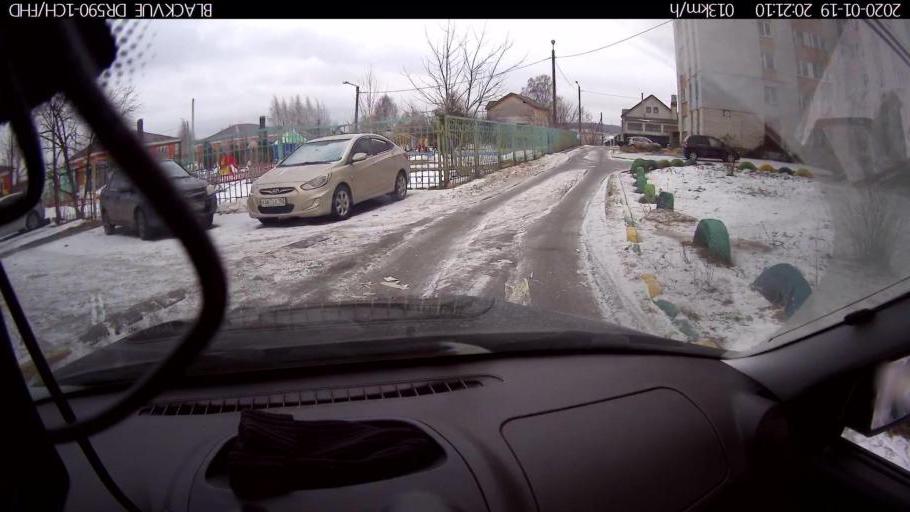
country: RU
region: Nizjnij Novgorod
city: Afonino
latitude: 56.2339
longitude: 44.0077
